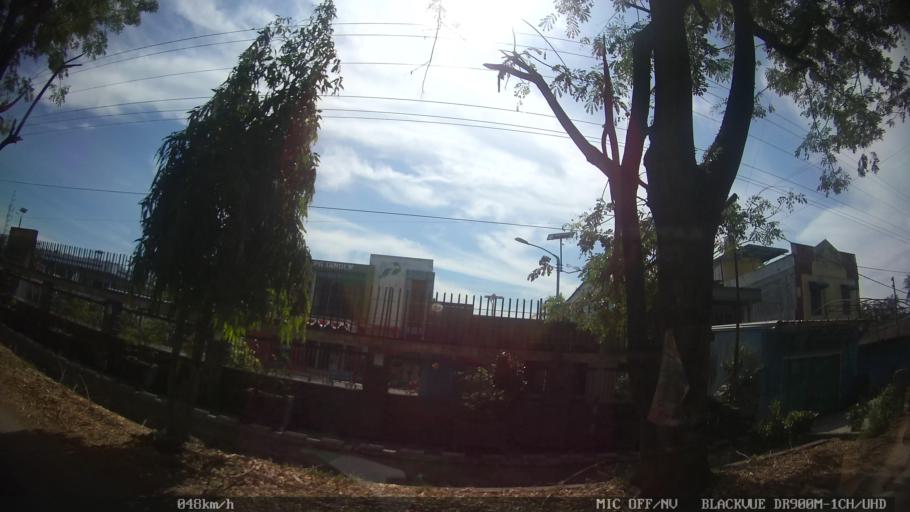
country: ID
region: North Sumatra
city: Binjai
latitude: 3.6684
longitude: 98.5097
